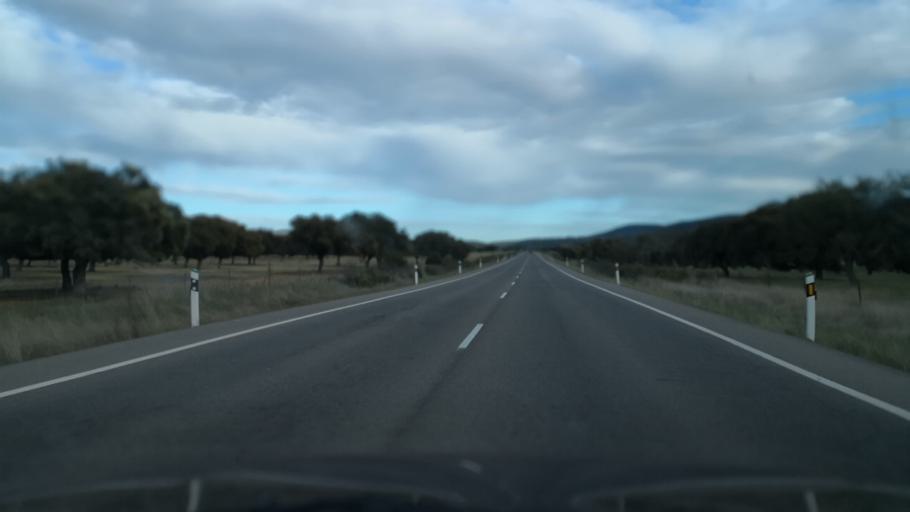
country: ES
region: Extremadura
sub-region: Provincia de Caceres
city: Pedroso de Acim
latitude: 39.8629
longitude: -6.4316
